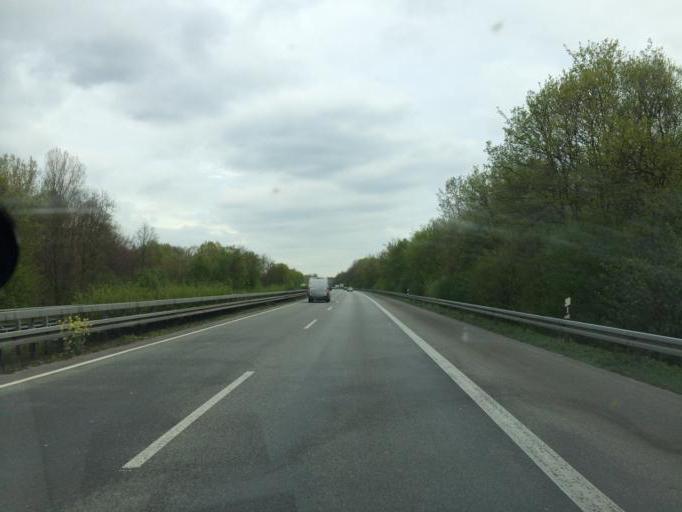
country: DE
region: North Rhine-Westphalia
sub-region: Regierungsbezirk Munster
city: Dulmen
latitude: 51.8286
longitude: 7.2347
